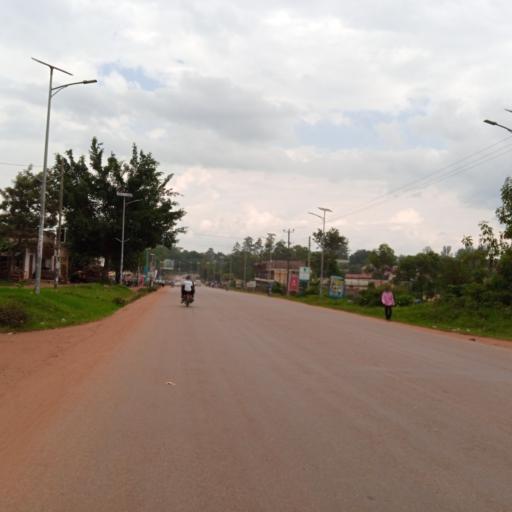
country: UG
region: Eastern Region
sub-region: Mbale District
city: Mbale
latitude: 1.0859
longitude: 34.1784
